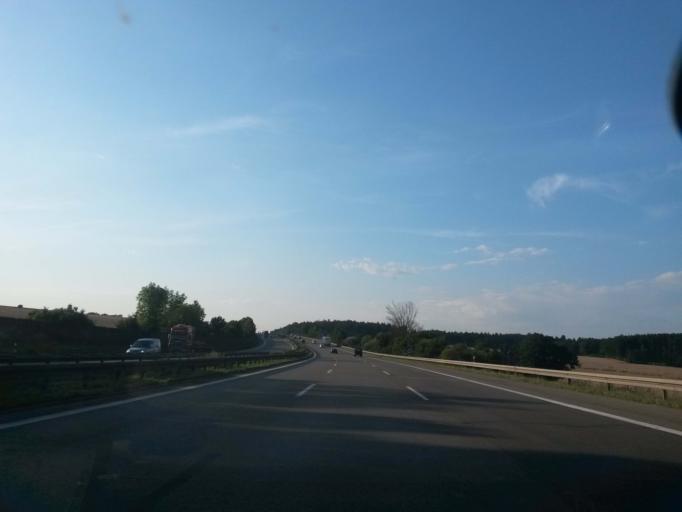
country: DE
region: Bavaria
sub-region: Upper Bavaria
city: Hepberg
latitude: 48.8292
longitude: 11.4730
